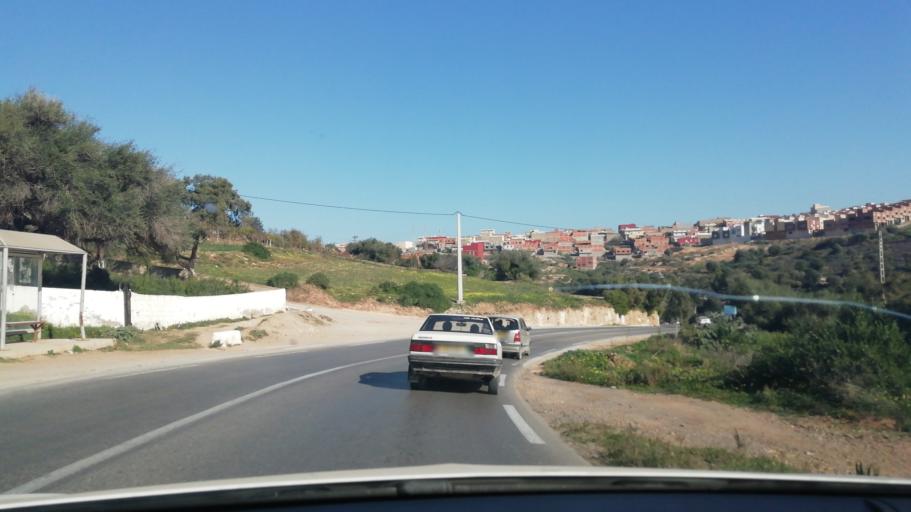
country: DZ
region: Tlemcen
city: Nedroma
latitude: 35.0850
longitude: -1.8717
